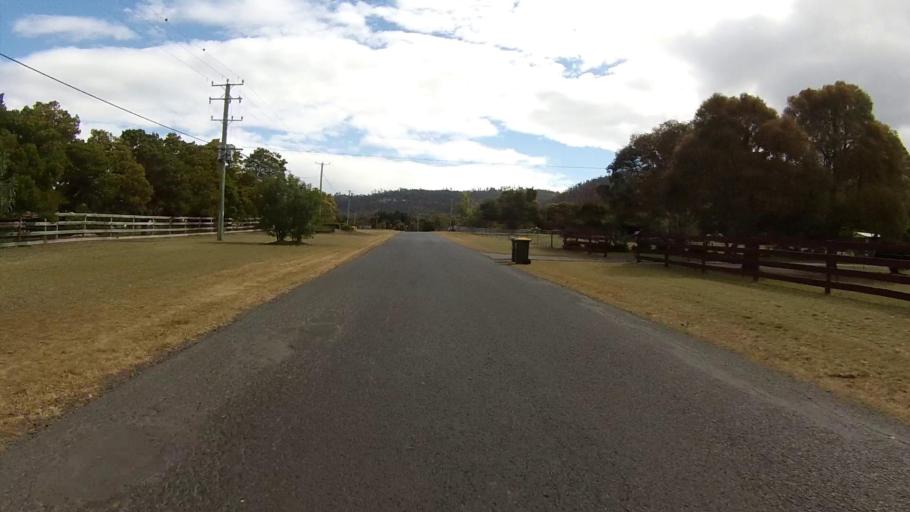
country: AU
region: Tasmania
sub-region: Clarence
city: Acton Park
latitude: -42.8645
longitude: 147.4852
